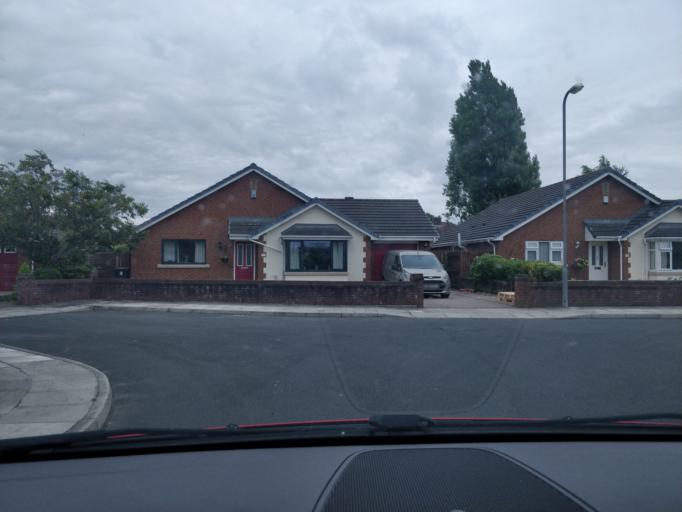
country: GB
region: England
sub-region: Sefton
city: Southport
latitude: 53.6657
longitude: -2.9724
